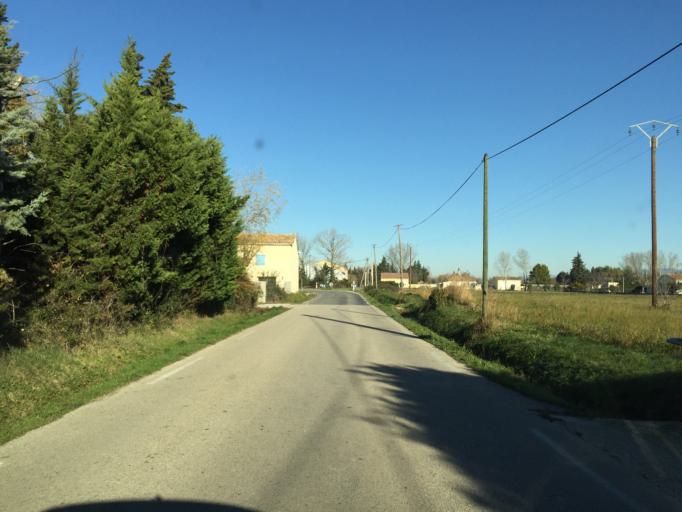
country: FR
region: Provence-Alpes-Cote d'Azur
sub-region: Departement du Vaucluse
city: Entraigues-sur-la-Sorgue
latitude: 44.0132
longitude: 4.9335
